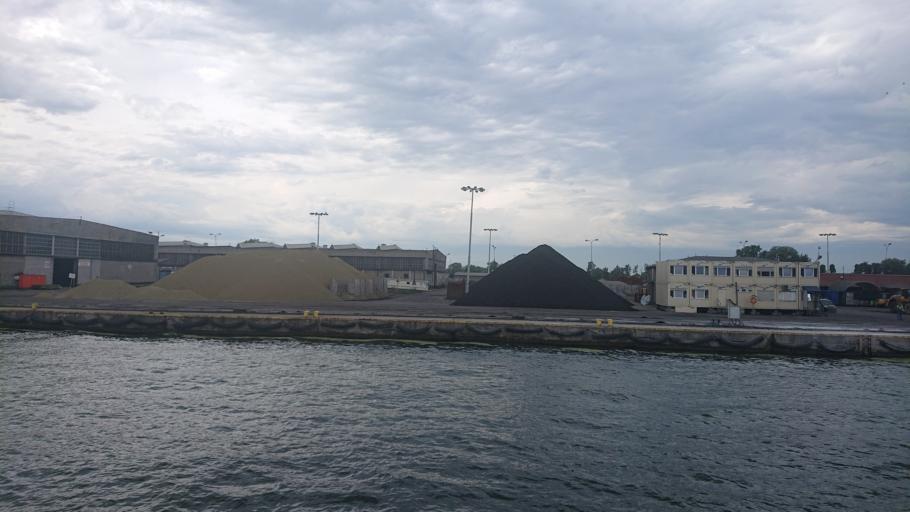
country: PL
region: Pomeranian Voivodeship
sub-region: Gdansk
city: Gdansk
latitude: 54.3890
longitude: 18.6678
